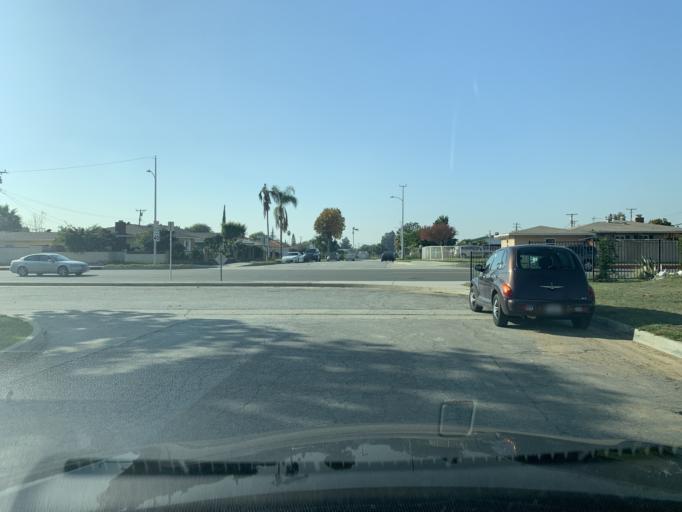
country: US
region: California
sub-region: Los Angeles County
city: Covina
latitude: 34.0747
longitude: -117.8985
